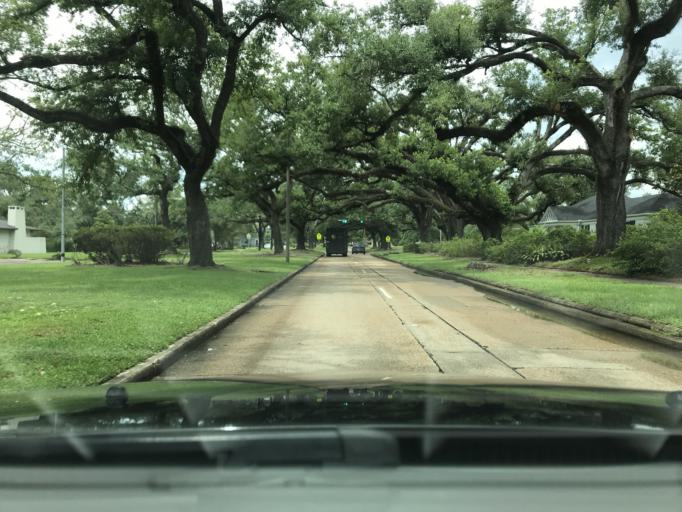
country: US
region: Louisiana
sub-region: Calcasieu Parish
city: Lake Charles
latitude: 30.2182
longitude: -93.2042
